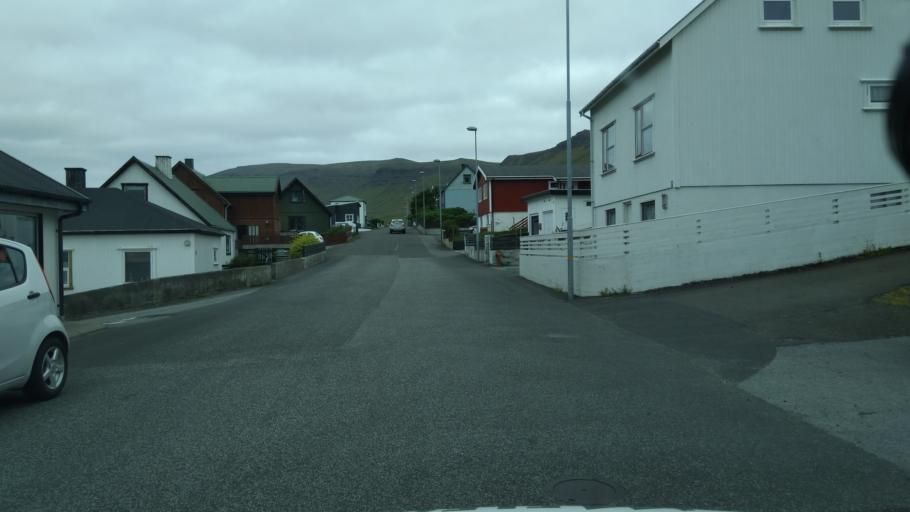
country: FO
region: Suduroy
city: Tvoroyri
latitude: 61.5622
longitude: -6.8311
